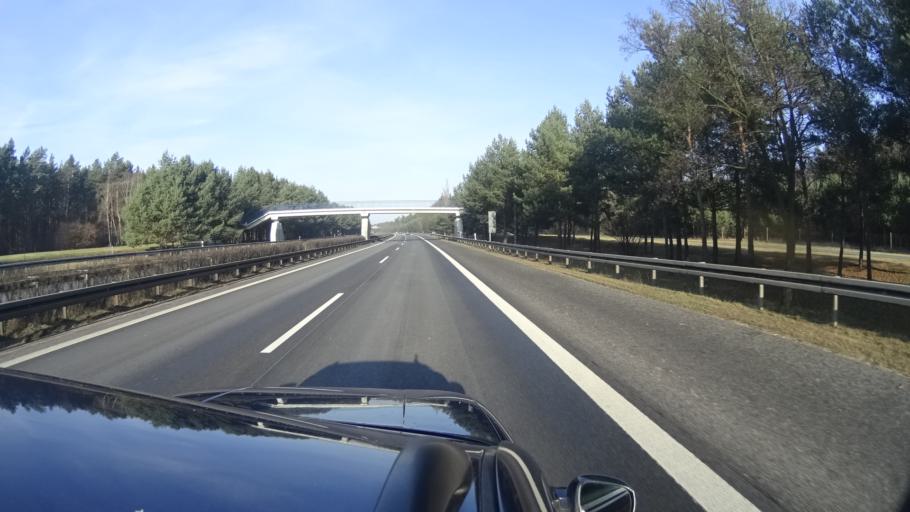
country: DE
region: Brandenburg
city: Hohen Neuendorf
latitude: 52.6598
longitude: 13.2434
